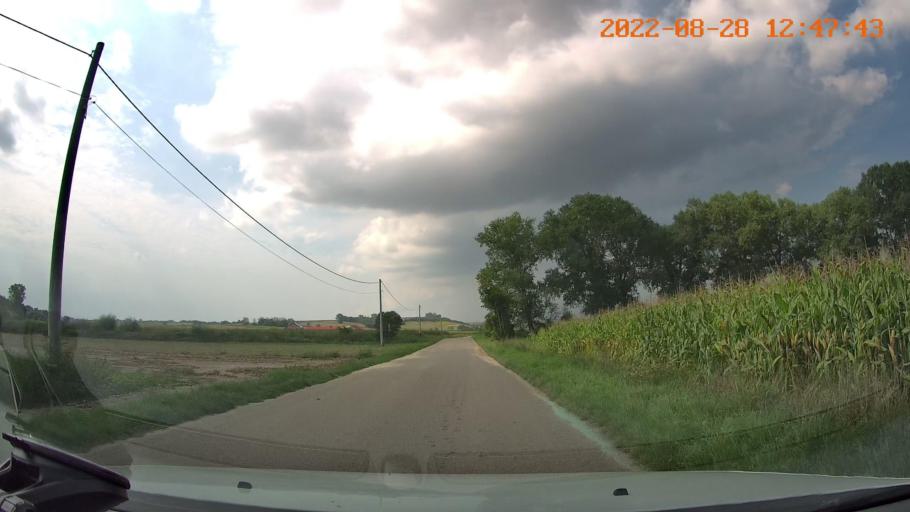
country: PL
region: Swietokrzyskie
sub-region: Powiat pinczowski
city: Dzialoszyce
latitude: 50.3578
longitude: 20.3061
